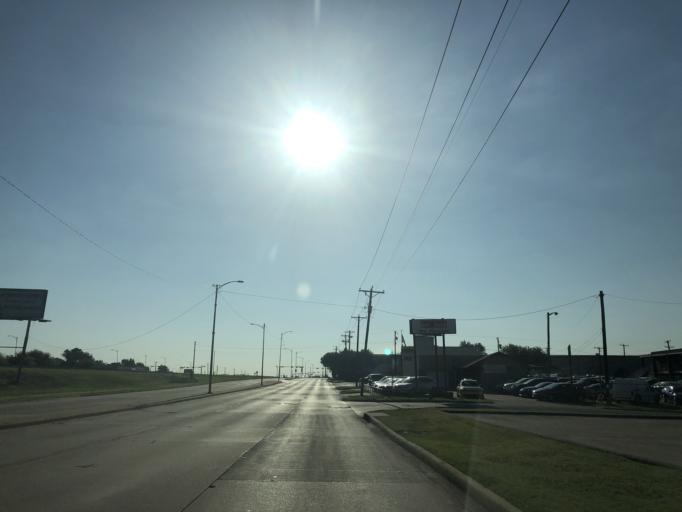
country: US
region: Texas
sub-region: Dallas County
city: Grand Prairie
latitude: 32.7401
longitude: -97.0269
